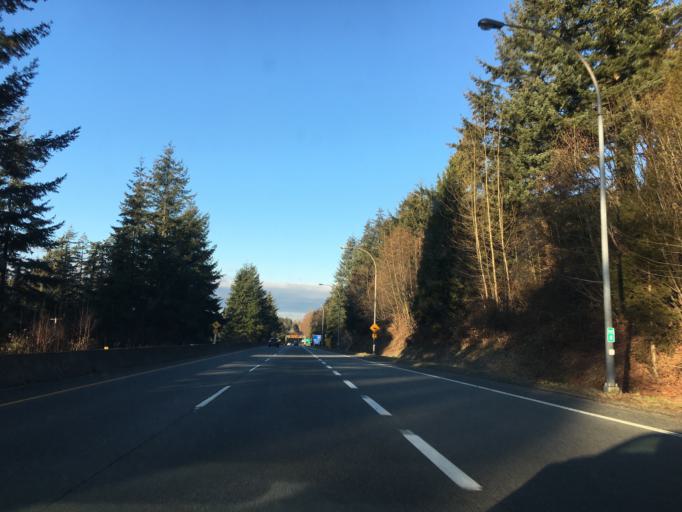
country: CA
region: British Columbia
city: West Vancouver
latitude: 49.3472
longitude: -123.2006
